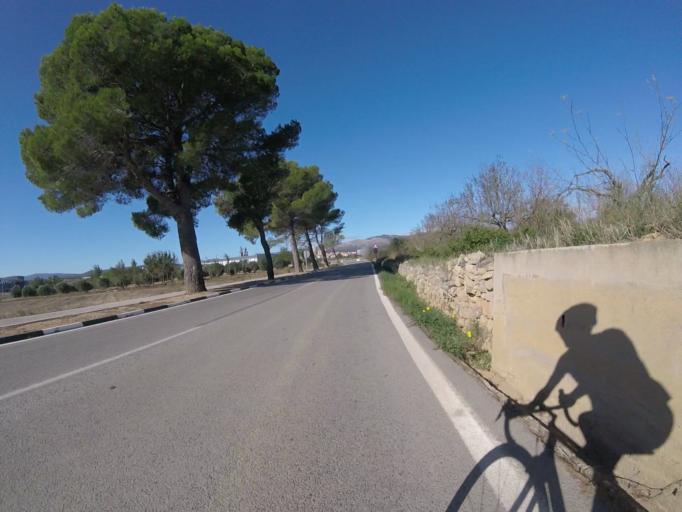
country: ES
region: Valencia
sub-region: Provincia de Castello
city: Chert/Xert
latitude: 40.4651
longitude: 0.1903
